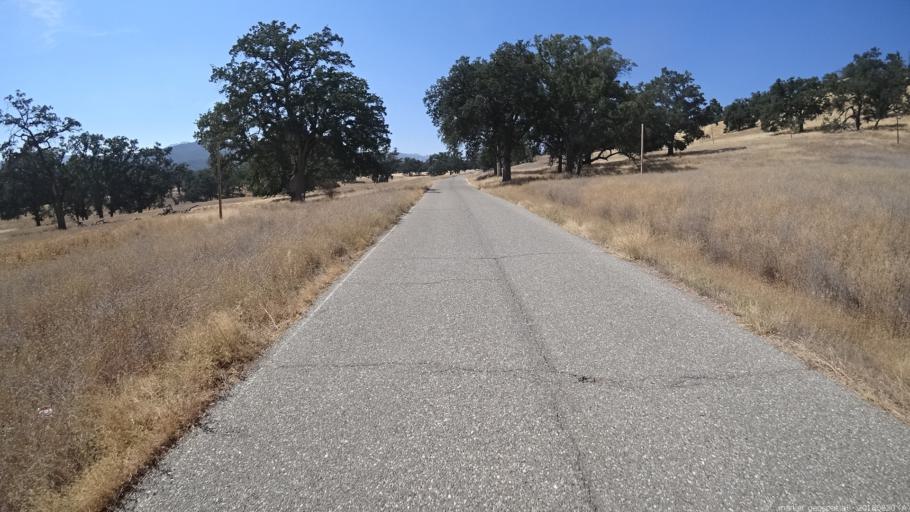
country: US
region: California
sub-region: Monterey County
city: Greenfield
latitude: 36.0761
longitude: -121.3763
